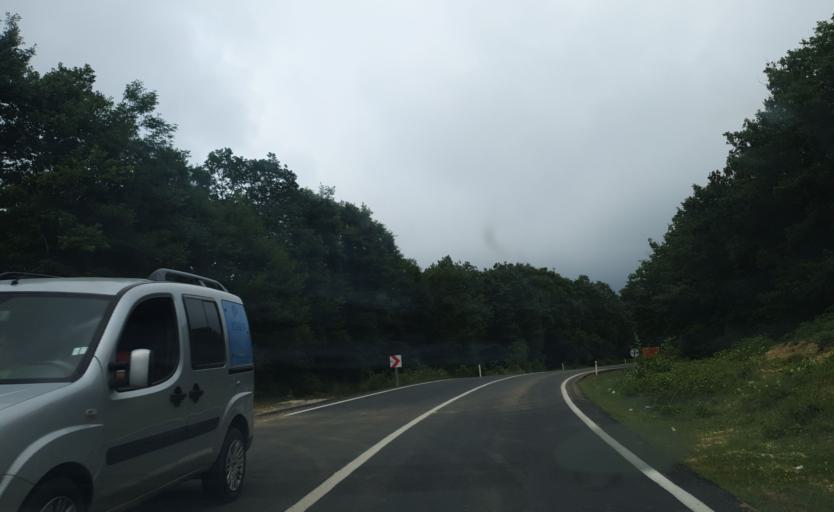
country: TR
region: Kirklareli
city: Salmydessus
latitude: 41.5935
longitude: 28.0764
